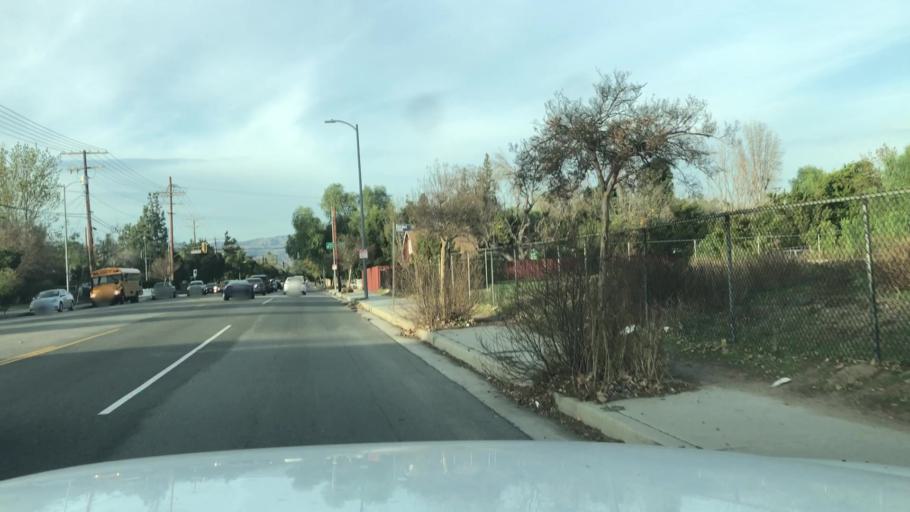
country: US
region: California
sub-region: Los Angeles County
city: Woodland Hills
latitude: 34.1707
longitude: -118.6145
